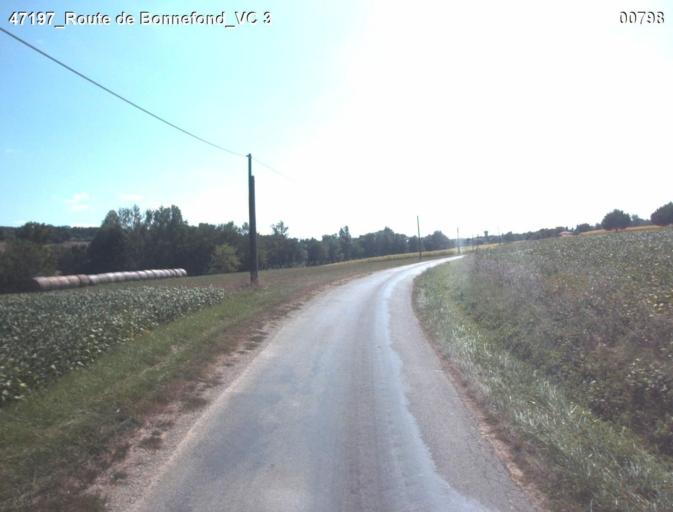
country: FR
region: Aquitaine
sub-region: Departement du Lot-et-Garonne
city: Laplume
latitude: 44.1024
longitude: 0.4759
